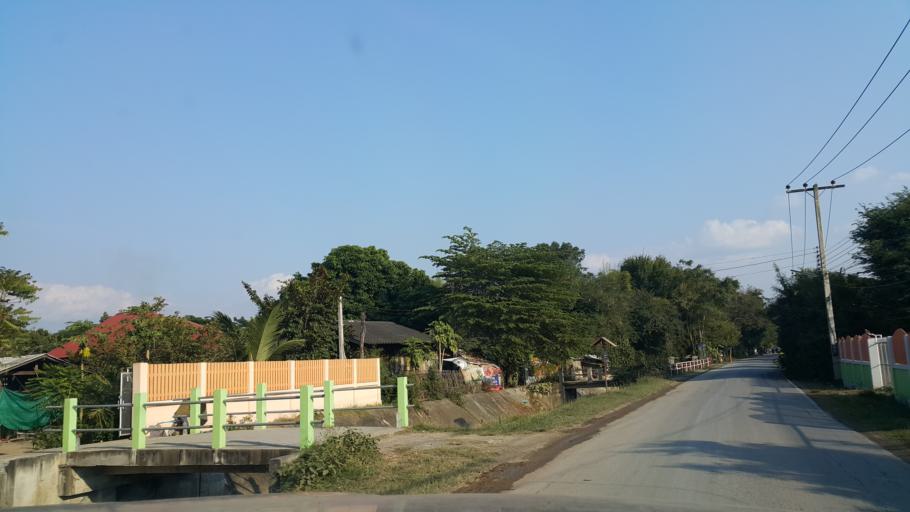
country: TH
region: Chiang Mai
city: San Kamphaeng
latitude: 18.7434
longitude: 99.1013
